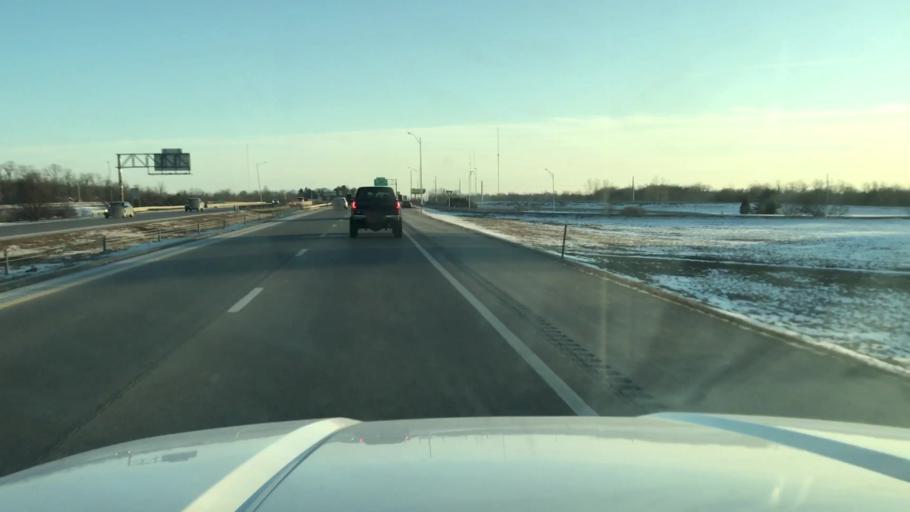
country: US
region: Missouri
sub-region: Buchanan County
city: Saint Joseph
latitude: 39.7512
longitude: -94.7900
